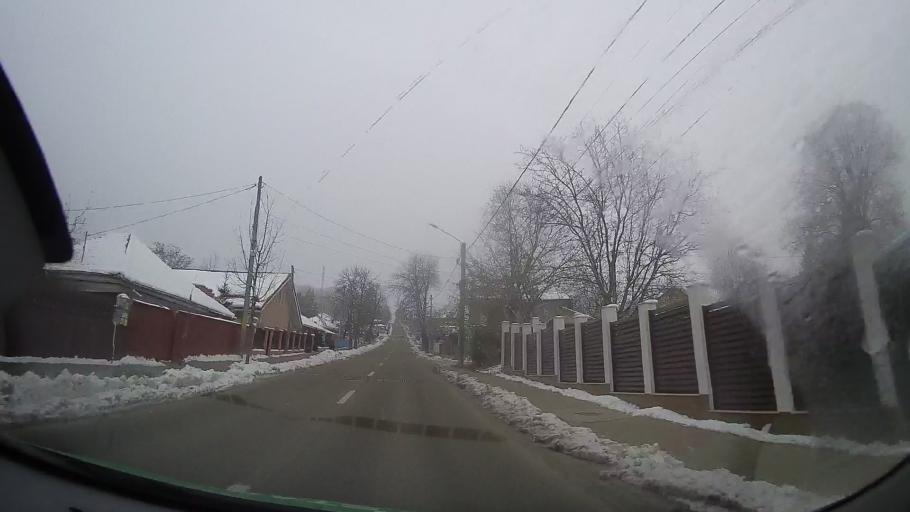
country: RO
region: Vaslui
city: Vaslui
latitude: 46.6489
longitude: 27.7285
